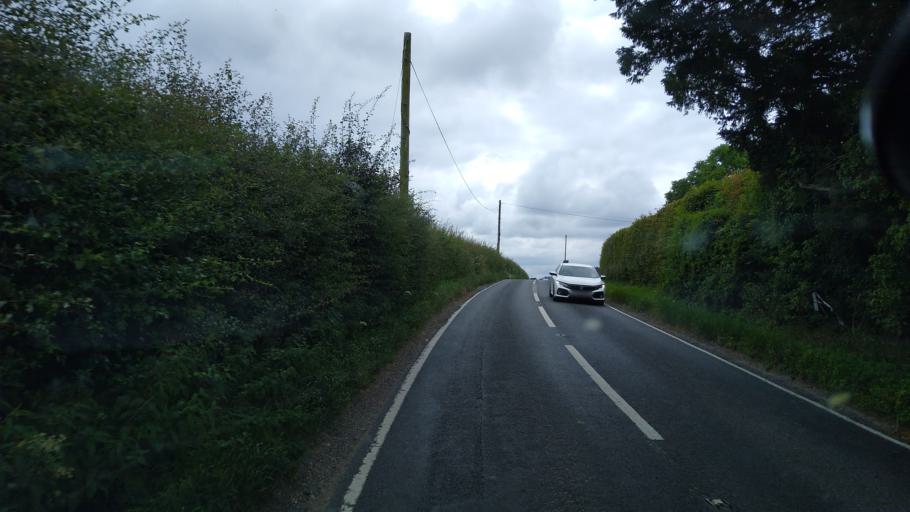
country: GB
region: England
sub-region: Hampshire
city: Alton
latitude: 51.1166
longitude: -0.9476
